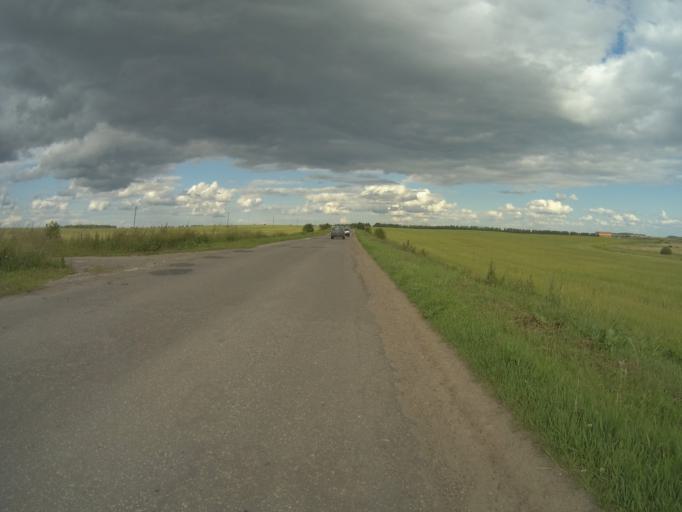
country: RU
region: Vladimir
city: Suzdal'
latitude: 56.3396
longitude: 40.4533
